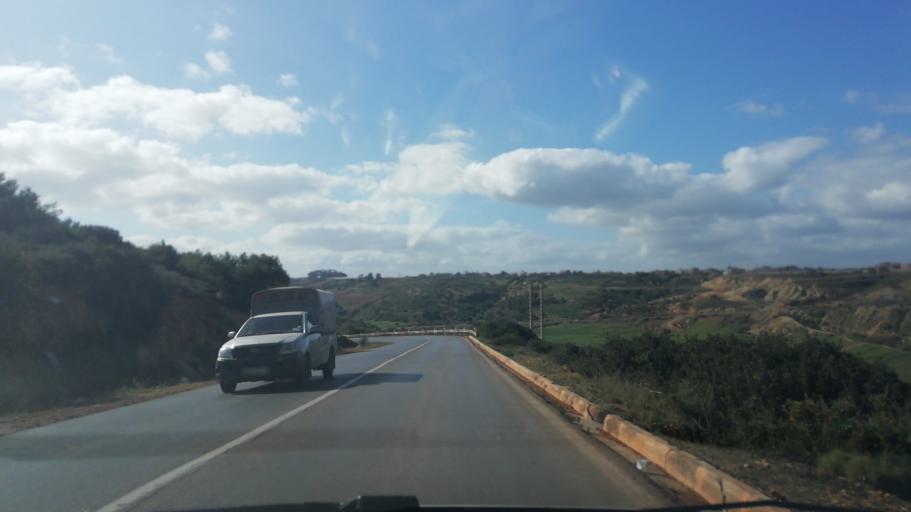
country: DZ
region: Relizane
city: Mazouna
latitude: 36.3237
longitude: 0.6858
